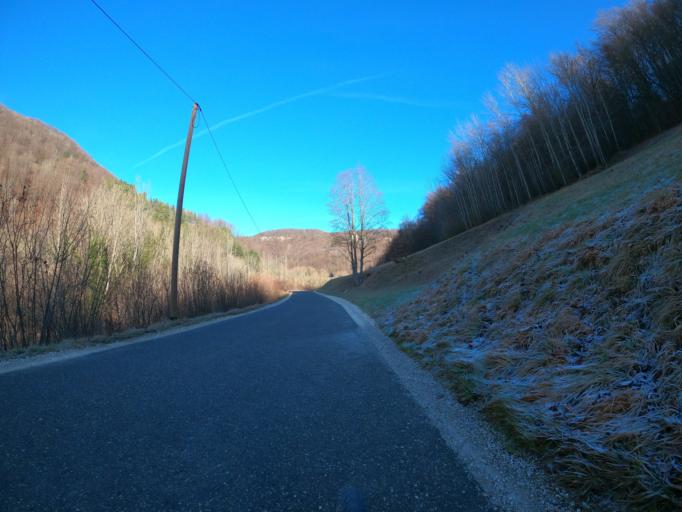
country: DE
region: Baden-Wuerttemberg
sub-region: Tuebingen Region
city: Eningen unter Achalm
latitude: 48.4457
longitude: 9.2777
